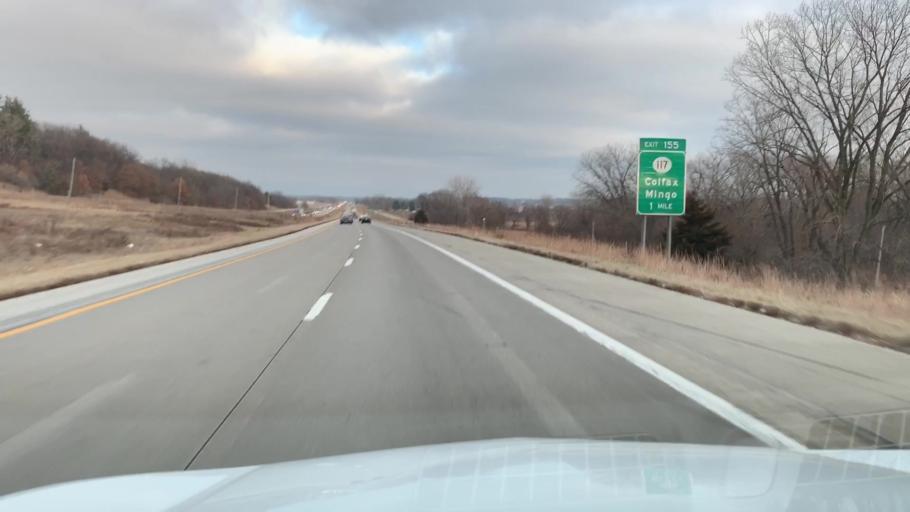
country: US
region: Iowa
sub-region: Jasper County
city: Colfax
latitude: 41.6861
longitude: -93.2748
